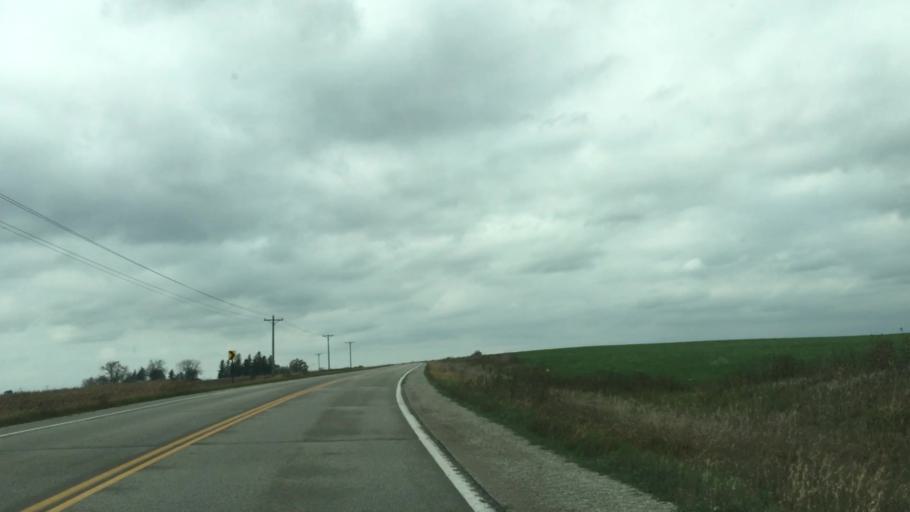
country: US
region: Minnesota
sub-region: Fillmore County
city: Preston
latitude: 43.7327
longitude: -92.0955
